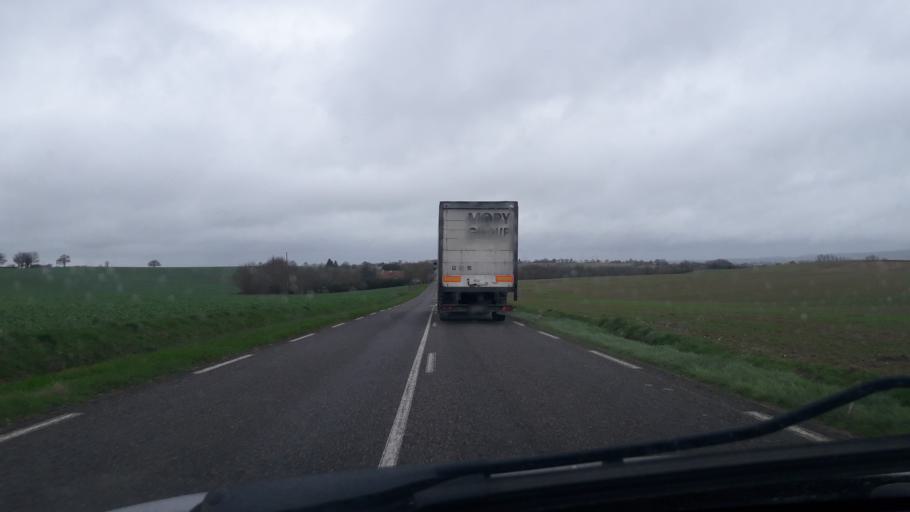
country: FR
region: Midi-Pyrenees
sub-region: Departement du Gers
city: Gimont
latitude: 43.7047
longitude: 0.9935
